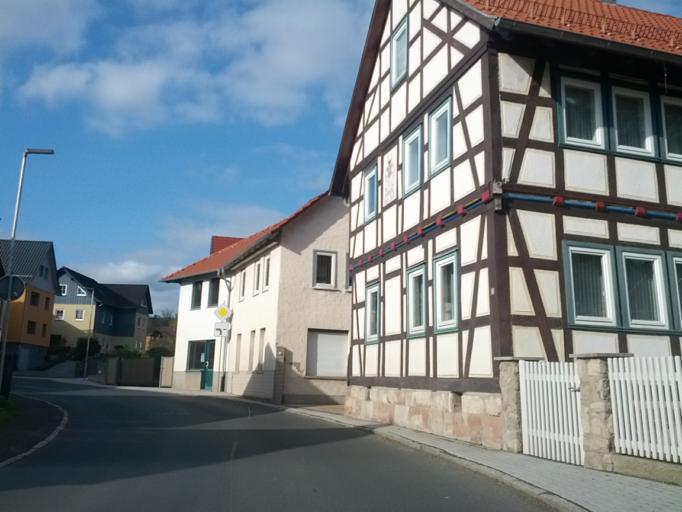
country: DE
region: Thuringia
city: Marksuhl
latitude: 50.9143
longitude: 10.2014
